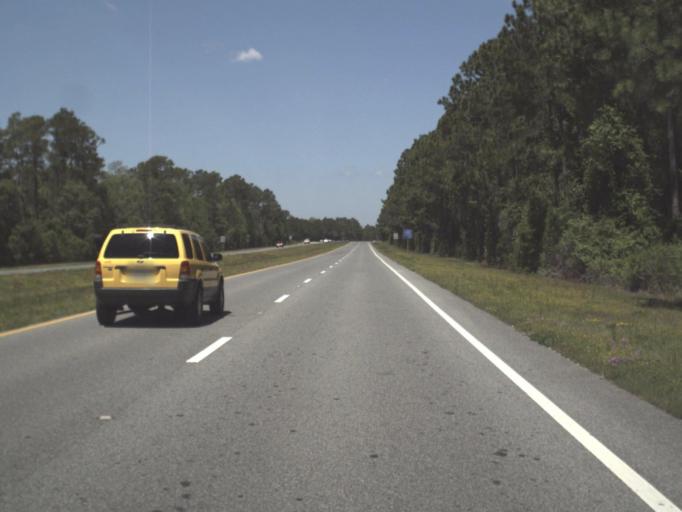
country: US
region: Florida
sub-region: Escambia County
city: Warrington
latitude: 30.3421
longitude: -87.3484
